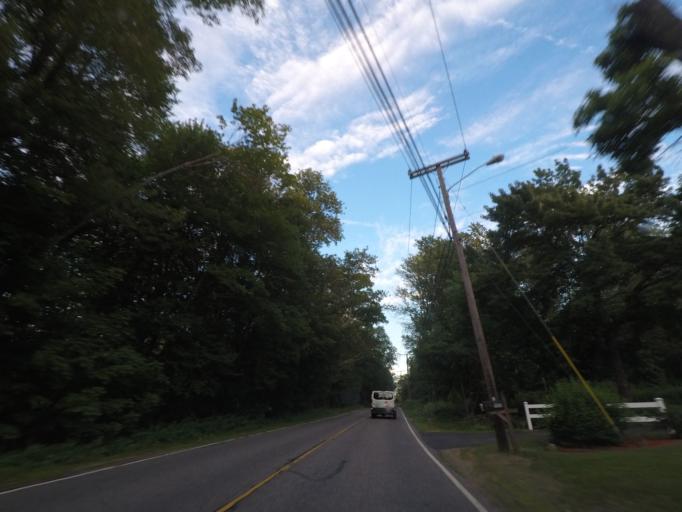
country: US
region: Massachusetts
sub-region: Worcester County
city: Warren
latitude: 42.1885
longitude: -72.1729
